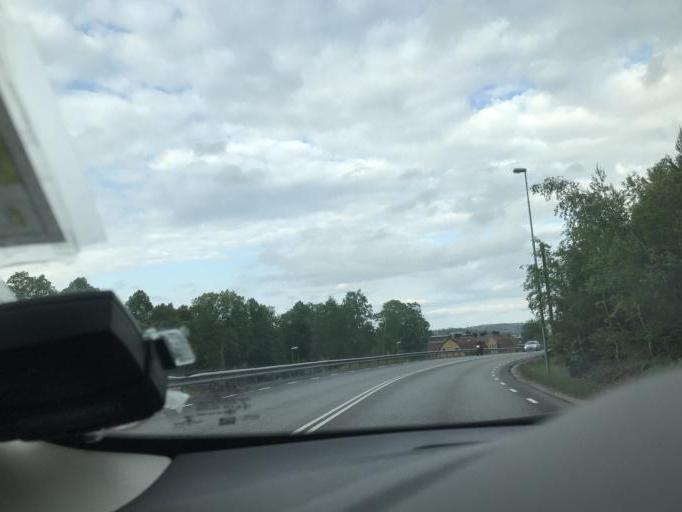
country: SE
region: Stockholm
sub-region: Botkyrka Kommun
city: Tumba
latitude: 59.2000
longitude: 17.8169
